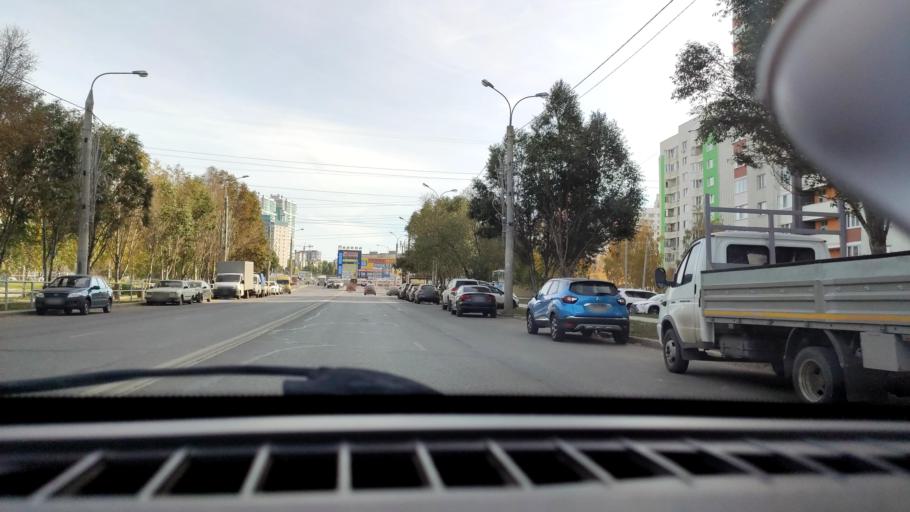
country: RU
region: Samara
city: Samara
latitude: 53.2599
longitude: 50.2102
